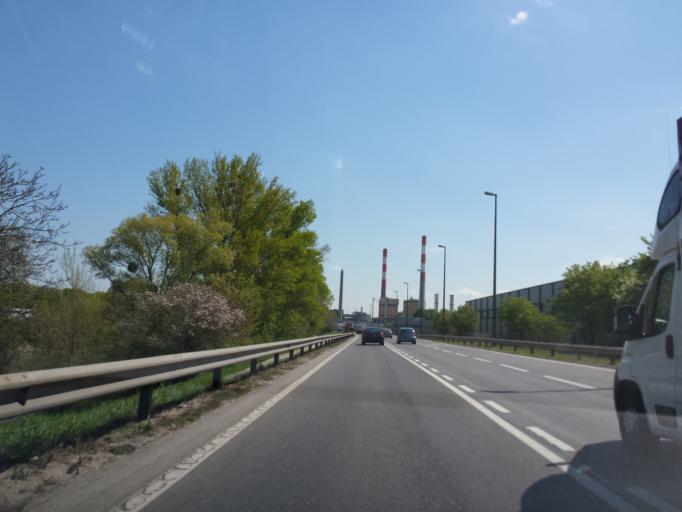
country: AT
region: Vienna
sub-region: Wien Stadt
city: Vienna
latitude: 48.1902
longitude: 16.4201
